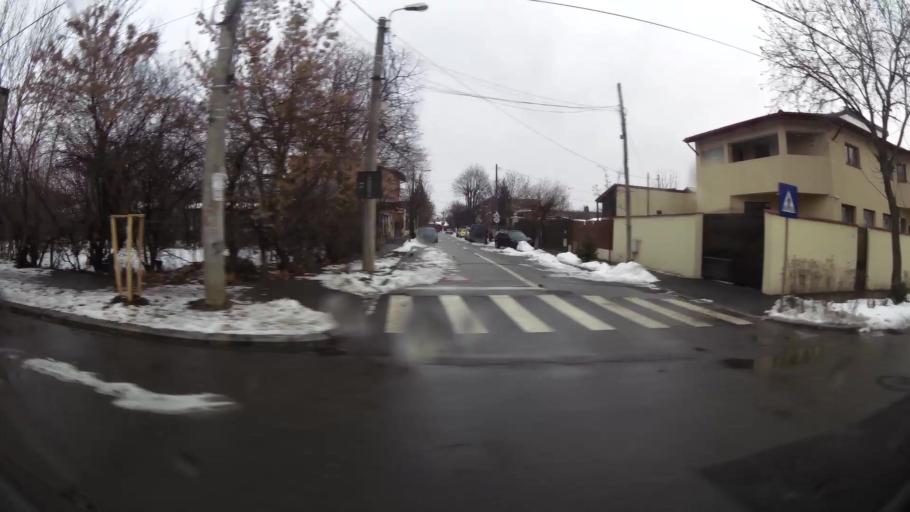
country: RO
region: Ilfov
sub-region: Comuna Chiajna
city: Rosu
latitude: 44.4889
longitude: 26.0215
